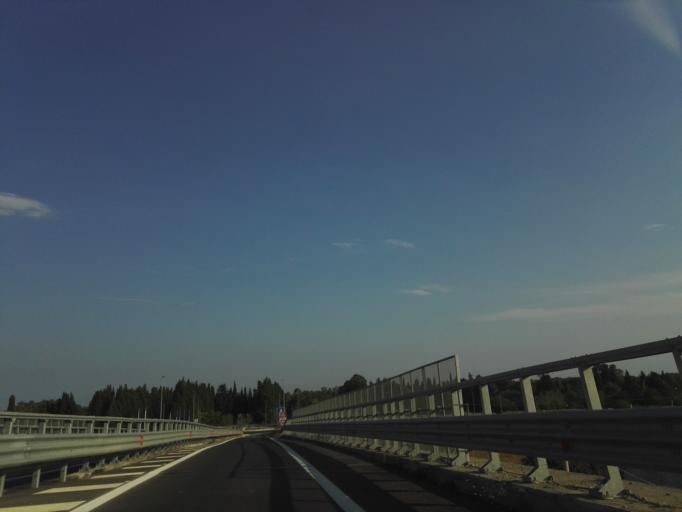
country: IT
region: Calabria
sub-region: Provincia di Reggio Calabria
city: Caulonia Marina
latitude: 38.3345
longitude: 16.4375
